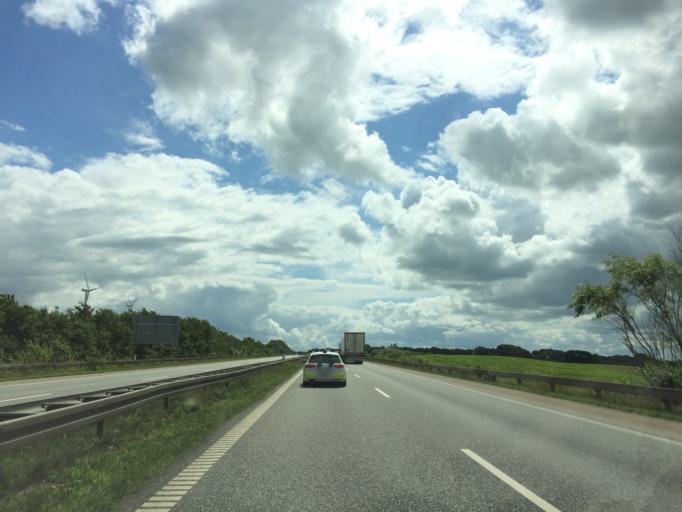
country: DK
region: North Denmark
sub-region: Mariagerfjord Kommune
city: Hobro
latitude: 56.7693
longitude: 9.6937
